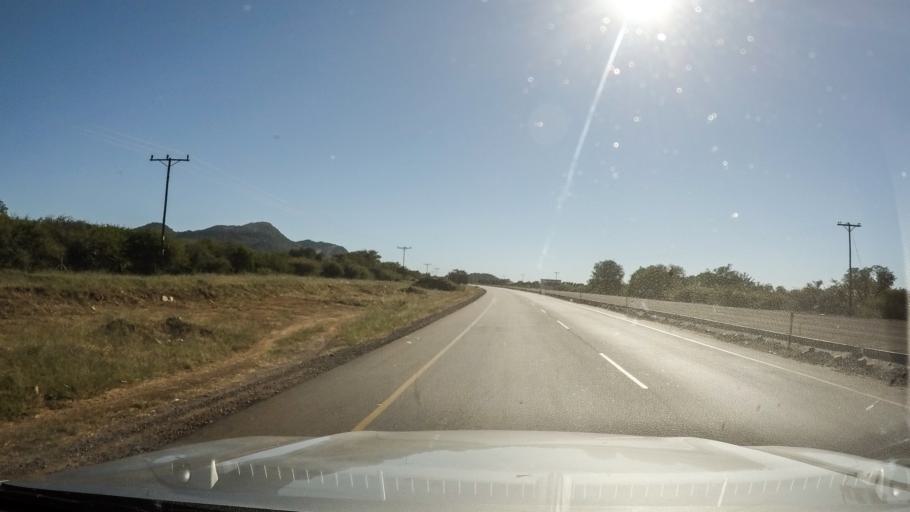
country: BW
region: South East
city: Gaborone
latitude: -24.7193
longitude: 25.8609
